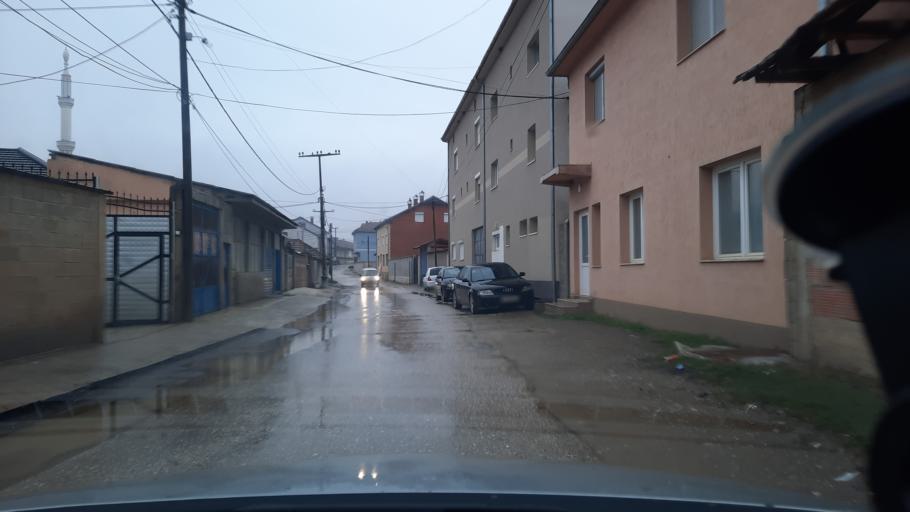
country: MK
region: Opstina Lipkovo
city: Lipkovo
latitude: 42.1577
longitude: 21.5835
